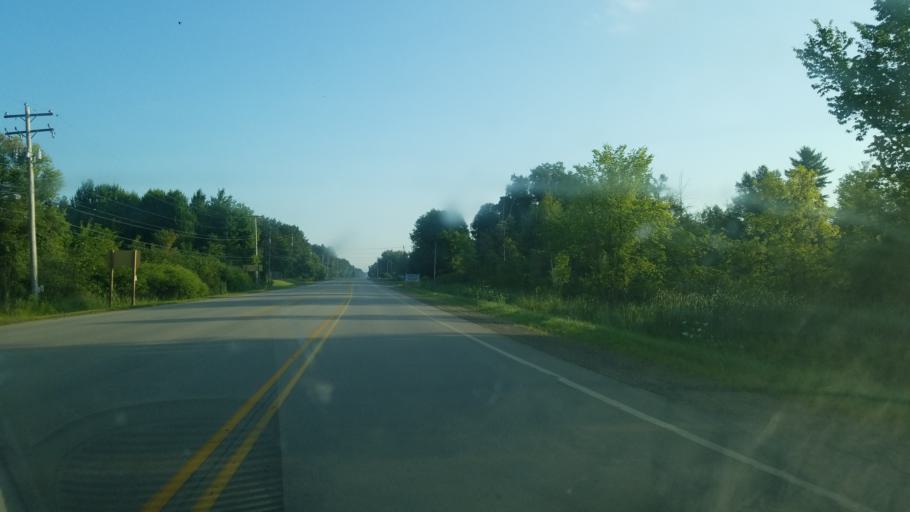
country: US
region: Michigan
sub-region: Montcalm County
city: Stanton
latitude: 43.2495
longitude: -85.0735
